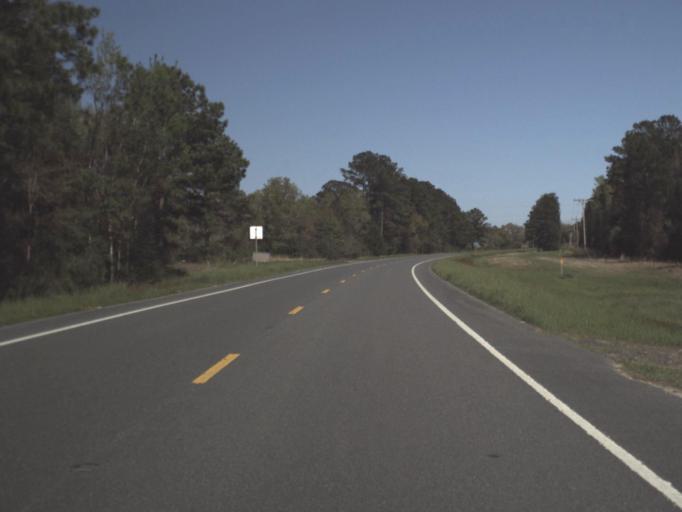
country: US
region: Florida
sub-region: Holmes County
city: Bonifay
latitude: 30.7615
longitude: -85.8704
